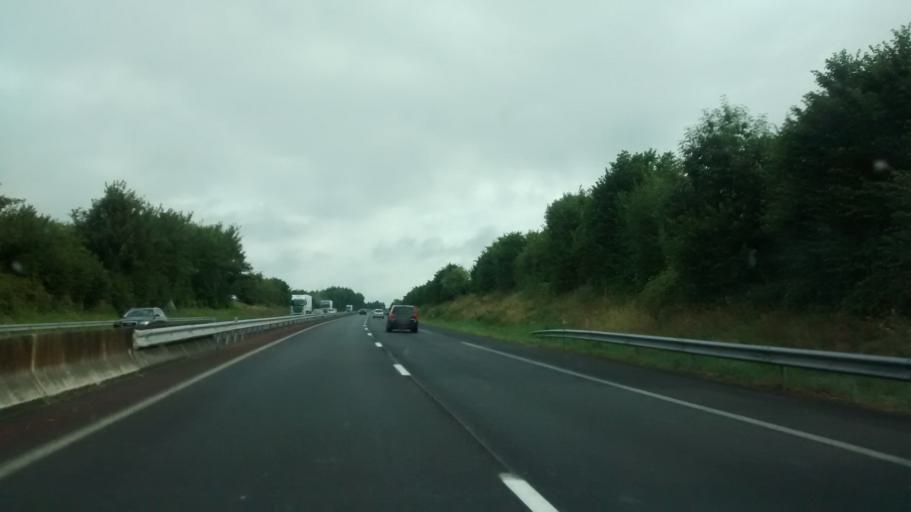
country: FR
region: Lower Normandy
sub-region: Departement de la Manche
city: Saint-James
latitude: 48.5569
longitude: -1.3410
